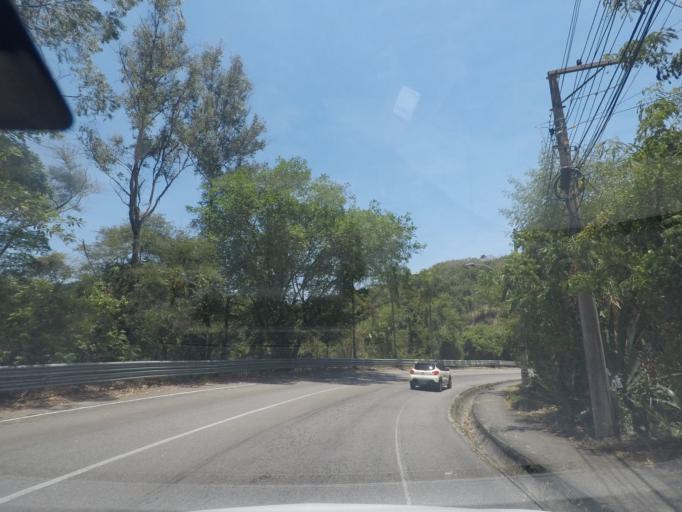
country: BR
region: Rio de Janeiro
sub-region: Niteroi
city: Niteroi
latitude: -22.9241
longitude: -43.0654
